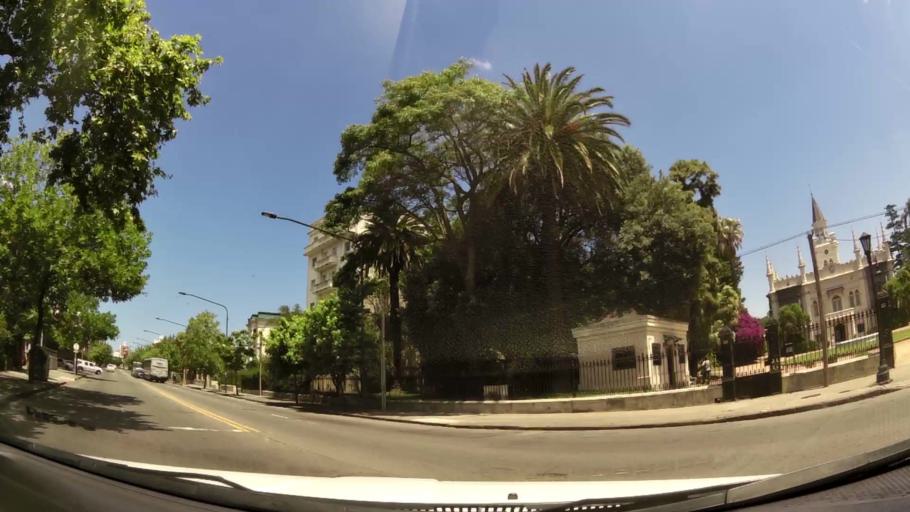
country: UY
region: Montevideo
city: Montevideo
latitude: -34.8694
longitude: -56.2049
